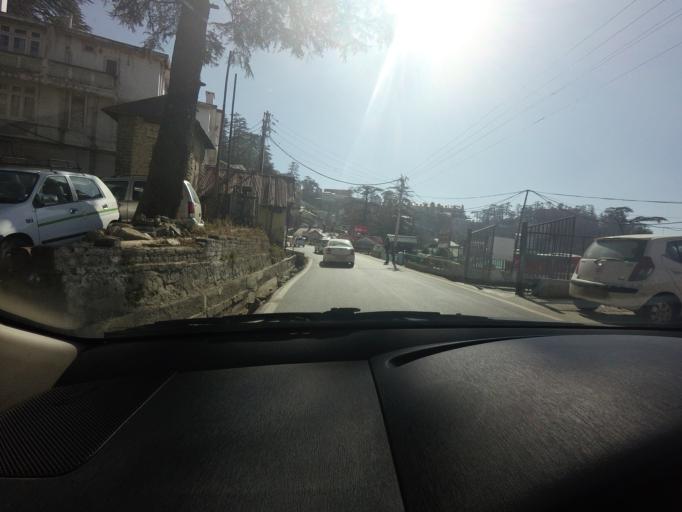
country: IN
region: Himachal Pradesh
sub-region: Shimla
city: Shimla
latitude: 31.1086
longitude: 77.1650
